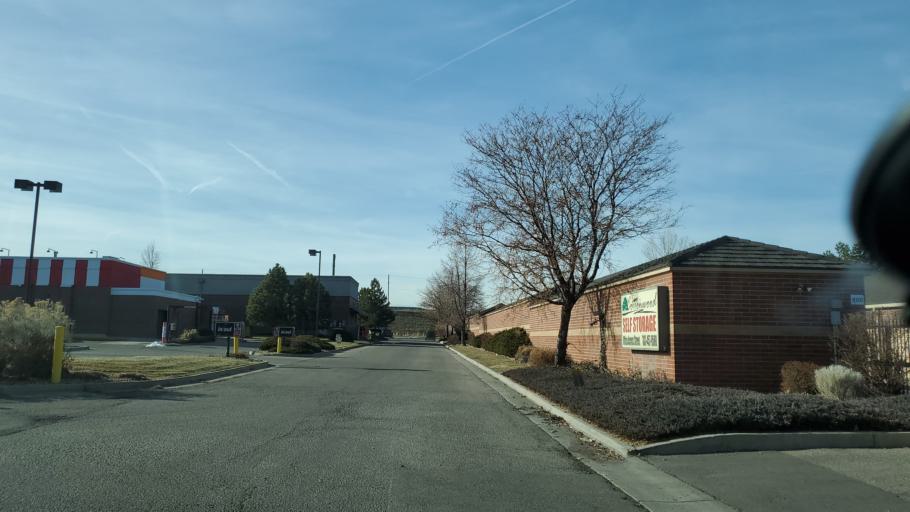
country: US
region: Colorado
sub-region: Adams County
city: Northglenn
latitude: 39.9148
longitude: -104.9558
